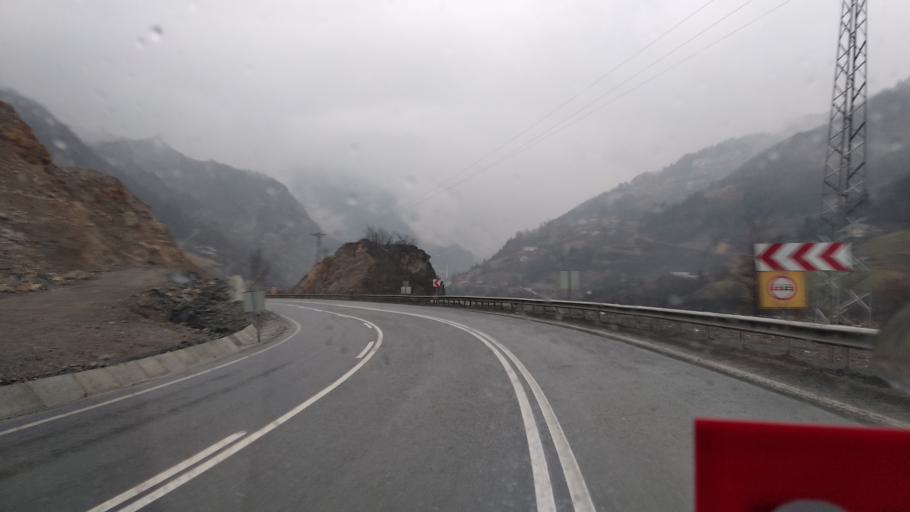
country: TR
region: Trabzon
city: Macka
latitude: 40.7139
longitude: 39.5142
